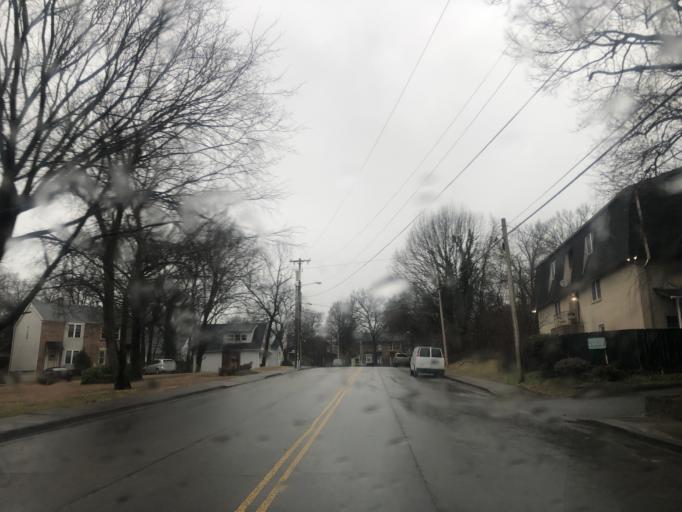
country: US
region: Tennessee
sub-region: Davidson County
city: Oak Hill
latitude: 36.1245
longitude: -86.8022
